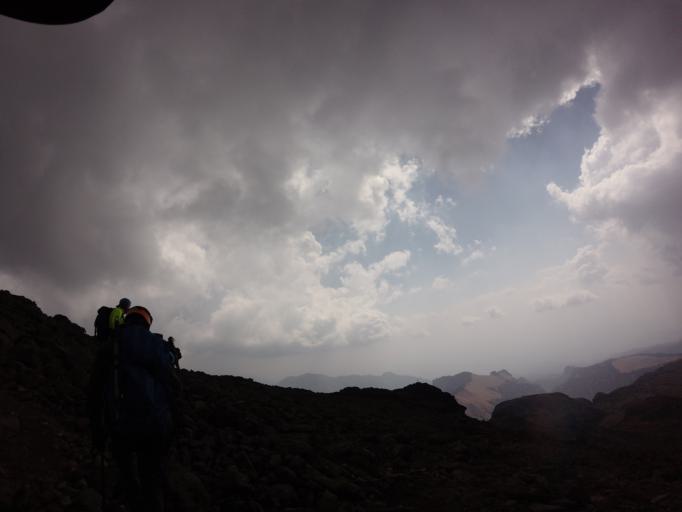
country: MX
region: Mexico
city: Amecameca de Juarez
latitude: 19.1538
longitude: -98.6413
